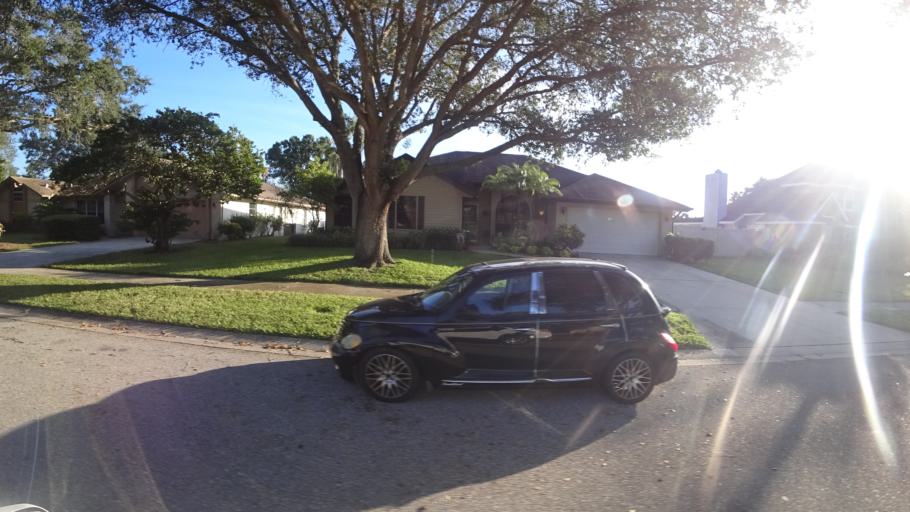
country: US
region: Florida
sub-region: Manatee County
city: Samoset
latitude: 27.4534
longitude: -82.5219
